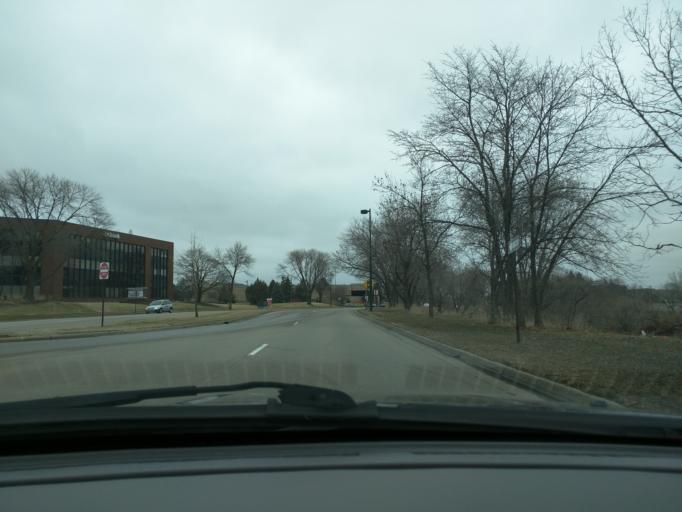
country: US
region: Minnesota
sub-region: Hennepin County
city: Eden Prairie
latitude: 44.8561
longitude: -93.4204
